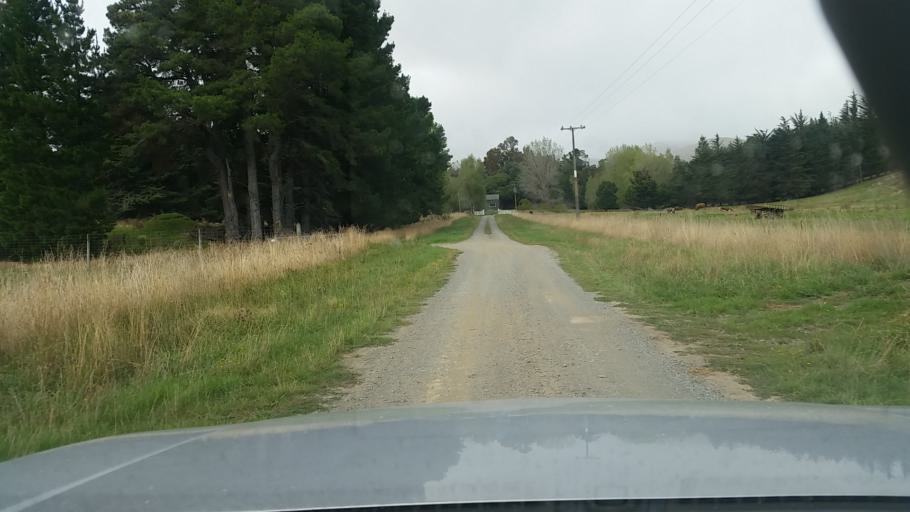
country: NZ
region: Marlborough
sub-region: Marlborough District
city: Blenheim
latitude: -41.7315
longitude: 173.9224
